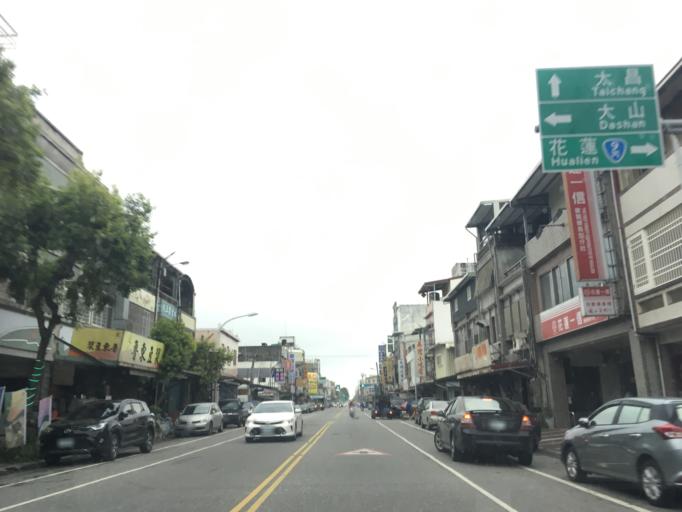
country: TW
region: Taiwan
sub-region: Hualien
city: Hualian
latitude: 23.9784
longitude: 121.5664
